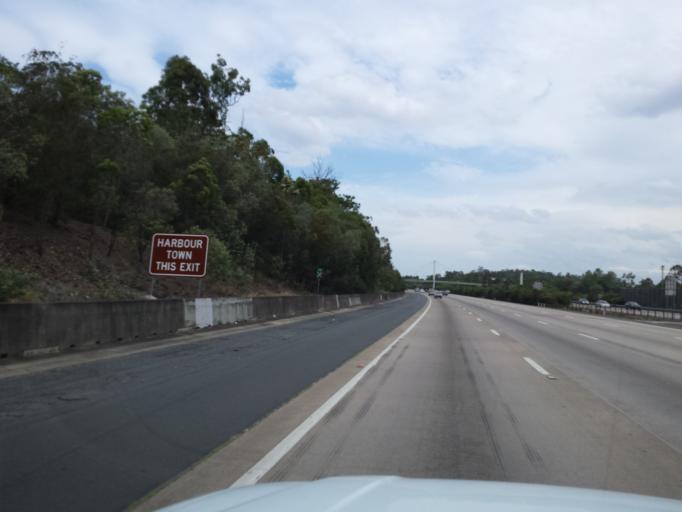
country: AU
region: Queensland
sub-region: Gold Coast
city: Upper Coomera
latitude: -27.9172
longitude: 153.3216
